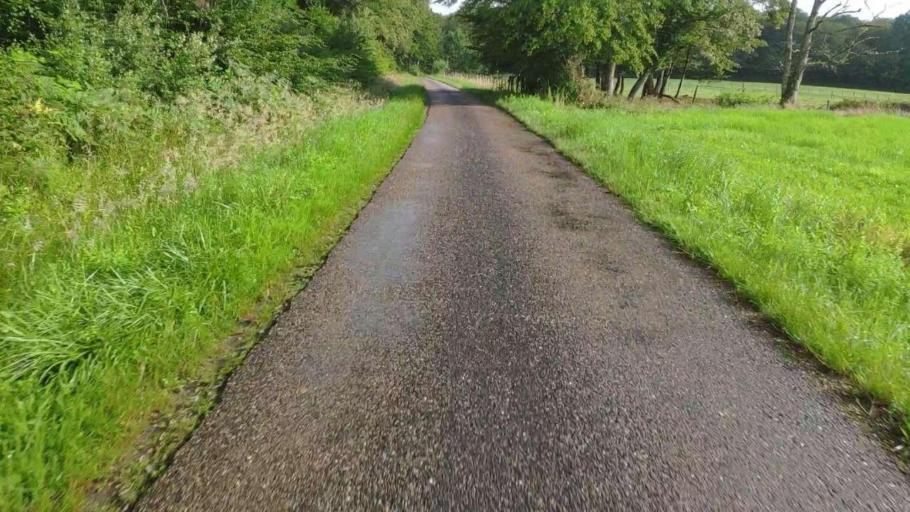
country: FR
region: Franche-Comte
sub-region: Departement du Jura
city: Mont-sous-Vaudrey
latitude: 46.8784
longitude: 5.5220
